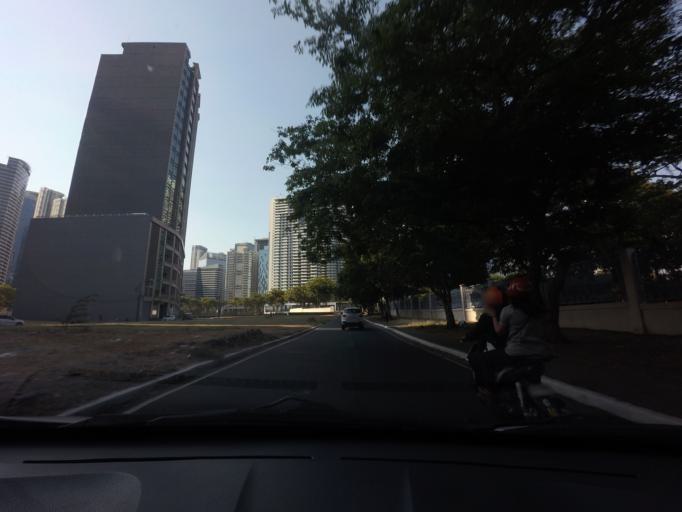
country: PH
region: Metro Manila
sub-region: Makati City
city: Makati City
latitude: 14.5436
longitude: 121.0477
